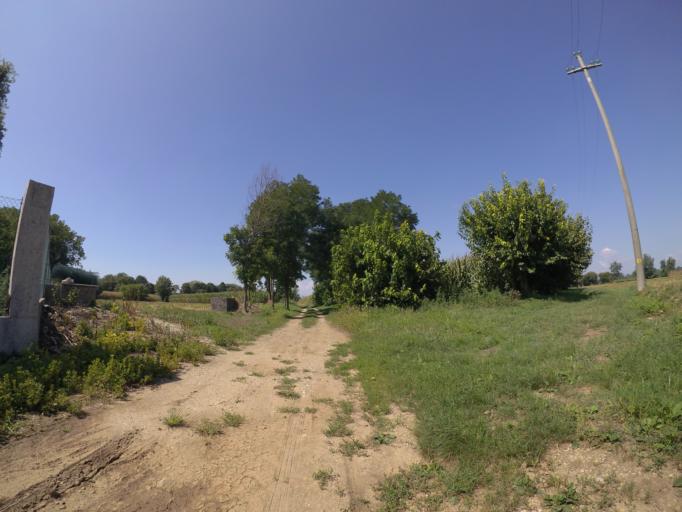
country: IT
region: Friuli Venezia Giulia
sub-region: Provincia di Udine
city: Talmassons
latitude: 45.9395
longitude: 13.0921
